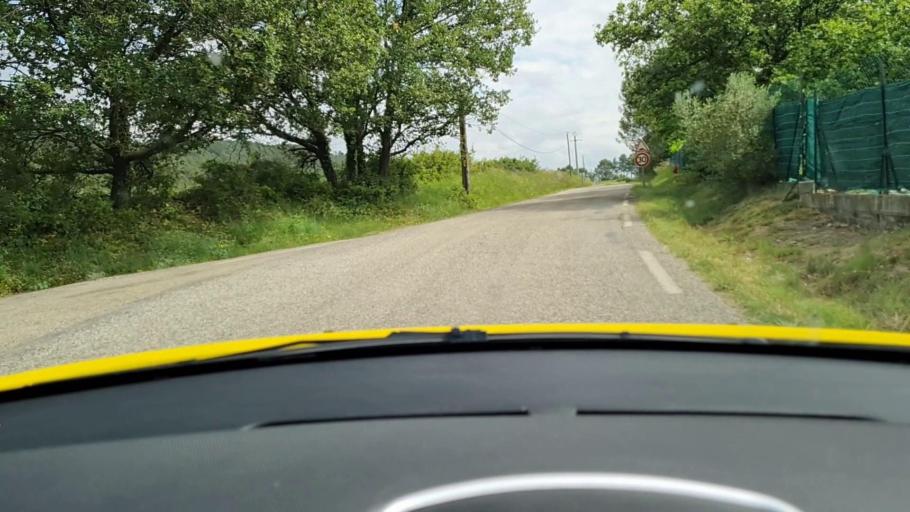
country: FR
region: Languedoc-Roussillon
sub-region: Departement du Gard
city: Quissac
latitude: 43.8479
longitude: 4.0057
